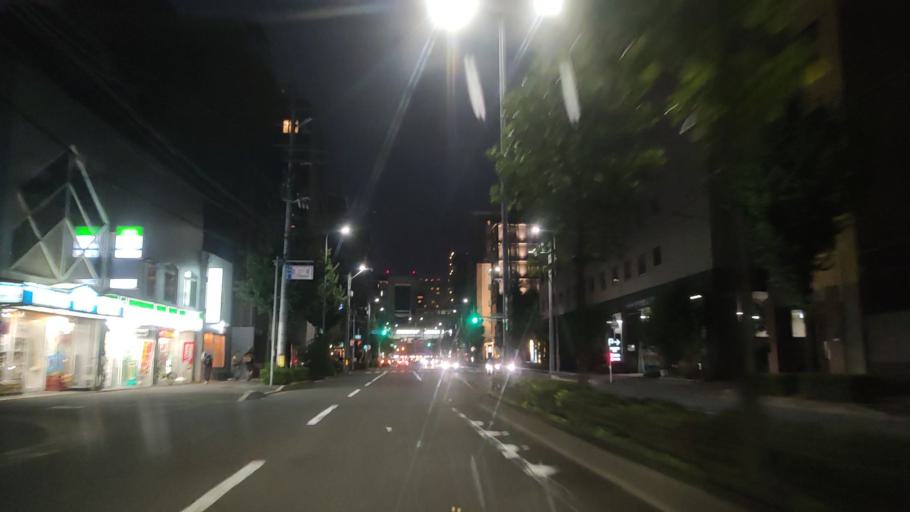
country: JP
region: Kyoto
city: Kyoto
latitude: 34.9811
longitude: 135.7598
